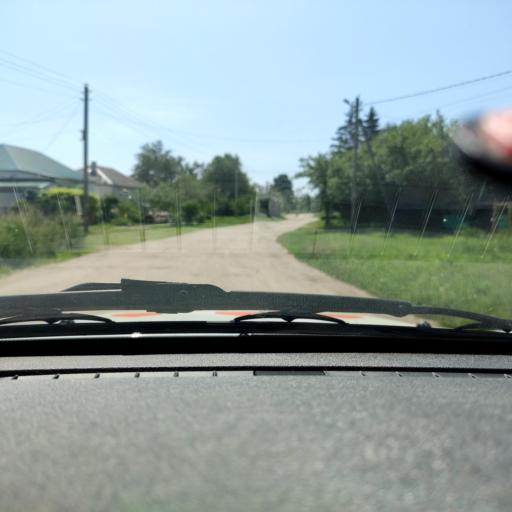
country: RU
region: Voronezj
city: Devitsa
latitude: 51.5955
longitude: 38.9907
